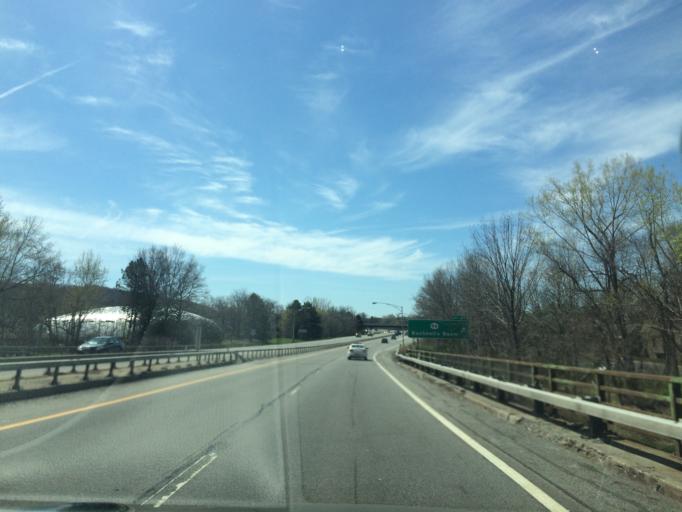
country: US
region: New York
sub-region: Monroe County
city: Fairport
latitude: 43.0625
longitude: -77.4716
